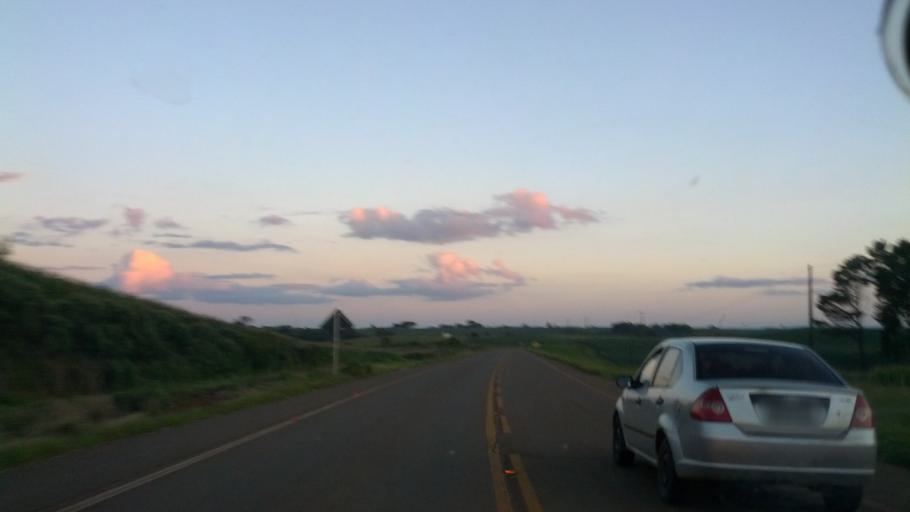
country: BR
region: Rio Grande do Sul
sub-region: Vacaria
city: Estrela
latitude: -27.8968
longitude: -50.7870
